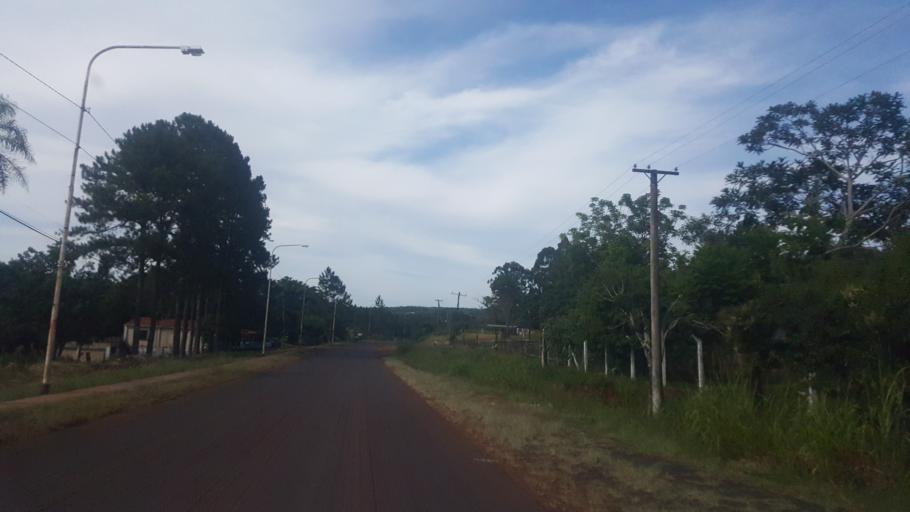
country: AR
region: Misiones
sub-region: Departamento de Leandro N. Alem
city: Leandro N. Alem
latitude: -27.5918
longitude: -55.3224
